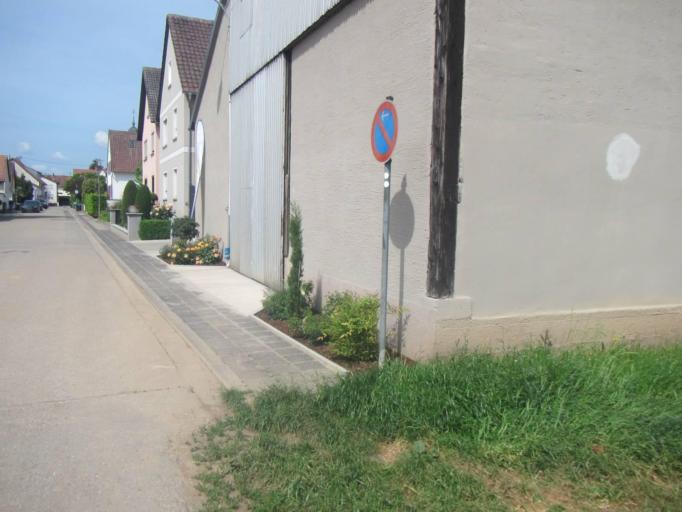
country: DE
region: Rheinland-Pfalz
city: Offenbach an der Queich
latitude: 49.1880
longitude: 8.1681
